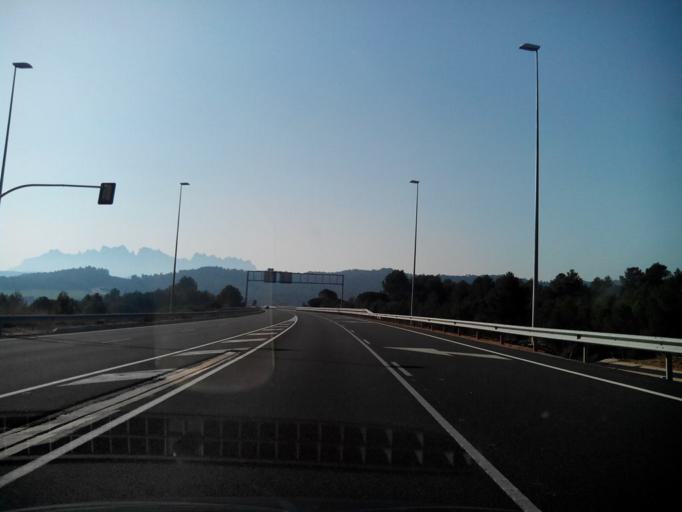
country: ES
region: Catalonia
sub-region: Provincia de Barcelona
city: Sant Joan de Vilatorrada
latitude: 41.7282
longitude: 1.7801
